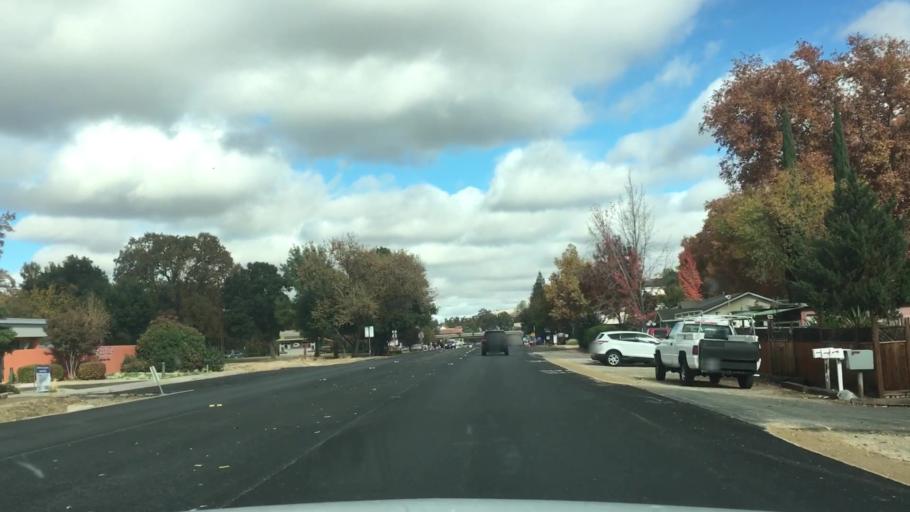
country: US
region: California
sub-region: San Luis Obispo County
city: Atascadero
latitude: 35.4817
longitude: -120.6661
